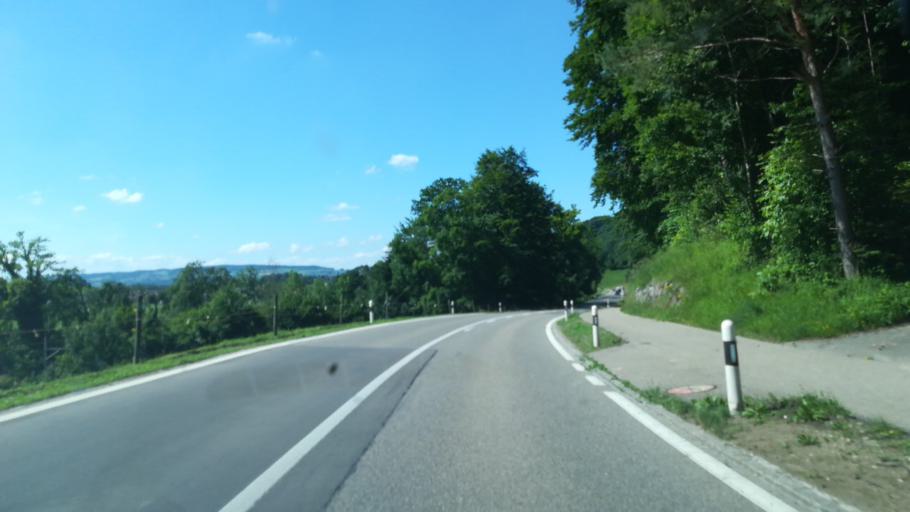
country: CH
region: Thurgau
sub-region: Weinfelden District
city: Sulgen
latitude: 47.5132
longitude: 9.2101
